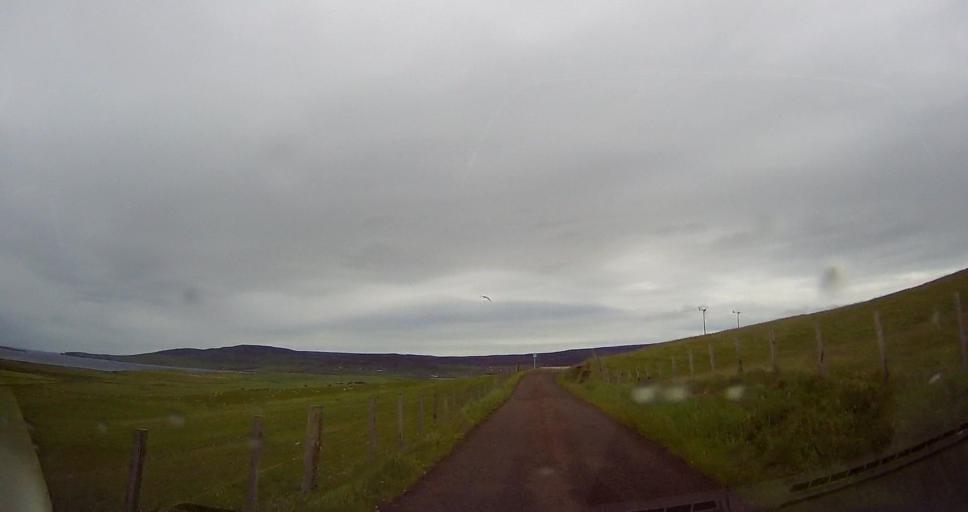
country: GB
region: Scotland
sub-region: Orkney Islands
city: Orkney
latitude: 59.1086
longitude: -3.0816
